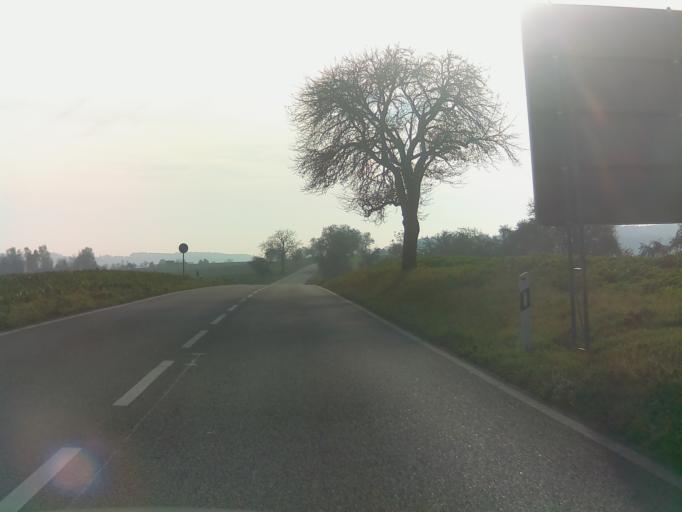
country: DE
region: Baden-Wuerttemberg
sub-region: Karlsruhe Region
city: Spechbach
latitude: 49.3632
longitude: 8.8690
